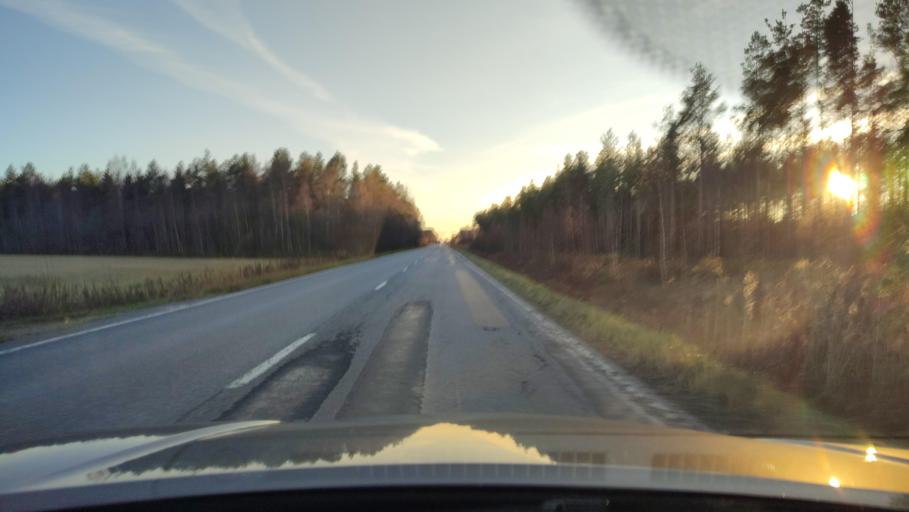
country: FI
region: Ostrobothnia
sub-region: Sydosterbotten
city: Naerpes
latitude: 62.5777
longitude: 21.4309
